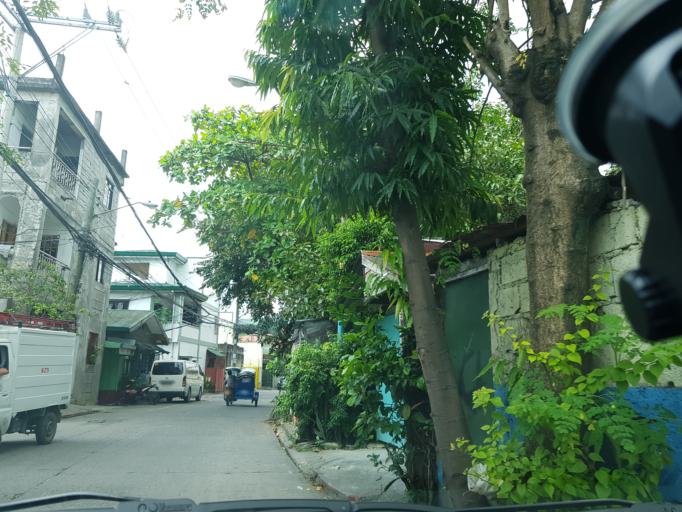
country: PH
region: Calabarzon
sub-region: Province of Rizal
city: Pateros
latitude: 14.5611
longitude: 121.0892
